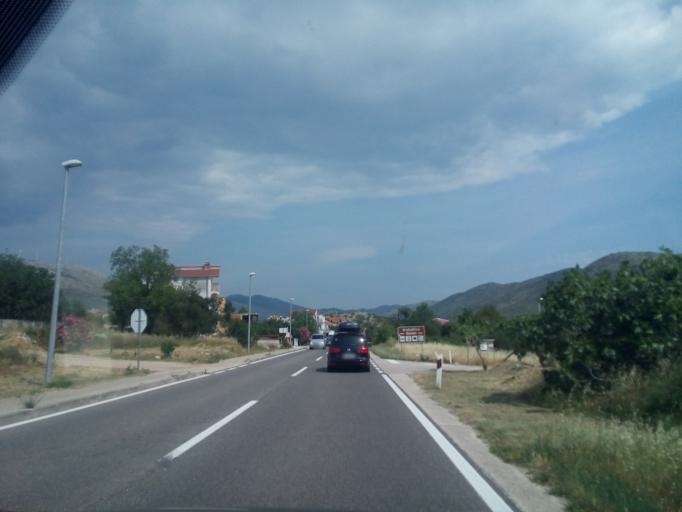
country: HR
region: Sibensko-Kniniska
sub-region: Grad Sibenik
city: Brodarica
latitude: 43.6356
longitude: 15.9688
